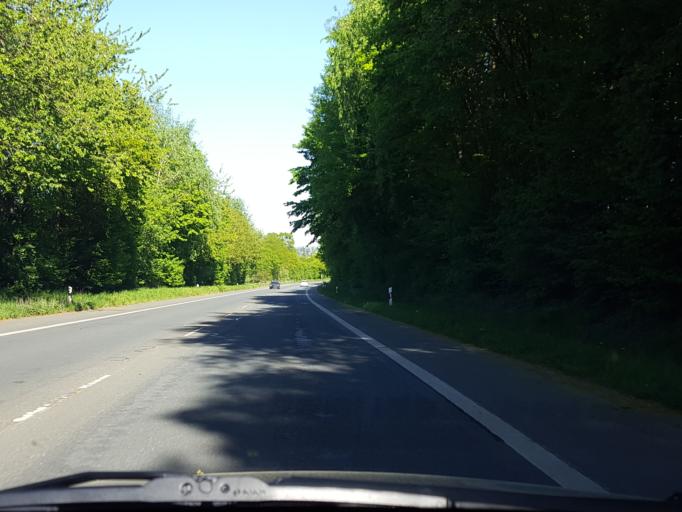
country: DE
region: North Rhine-Westphalia
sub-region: Regierungsbezirk Munster
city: Haltern
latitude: 51.7790
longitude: 7.2189
